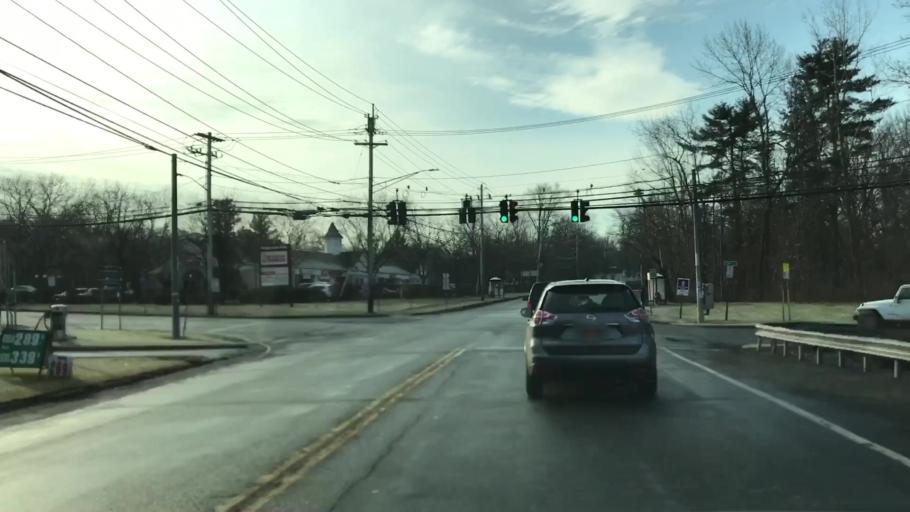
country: US
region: New York
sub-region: Rockland County
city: Congers
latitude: 41.1472
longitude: -73.9344
